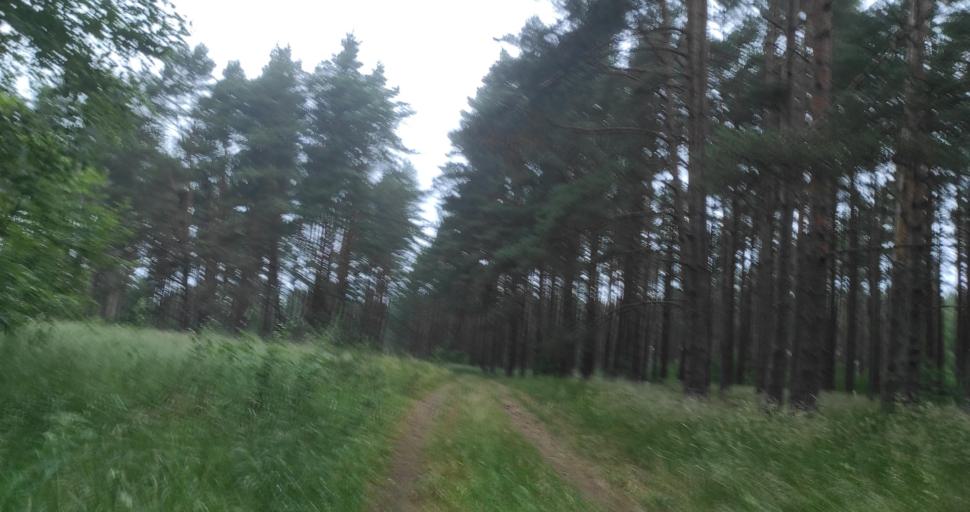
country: LV
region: Pavilostas
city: Pavilosta
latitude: 56.8872
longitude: 21.1965
